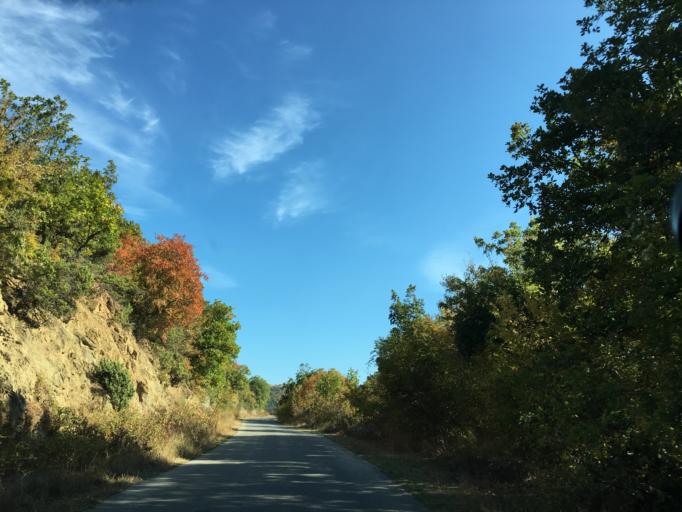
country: BG
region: Khaskovo
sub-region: Obshtina Ivaylovgrad
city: Ivaylovgrad
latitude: 41.4065
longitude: 26.1254
